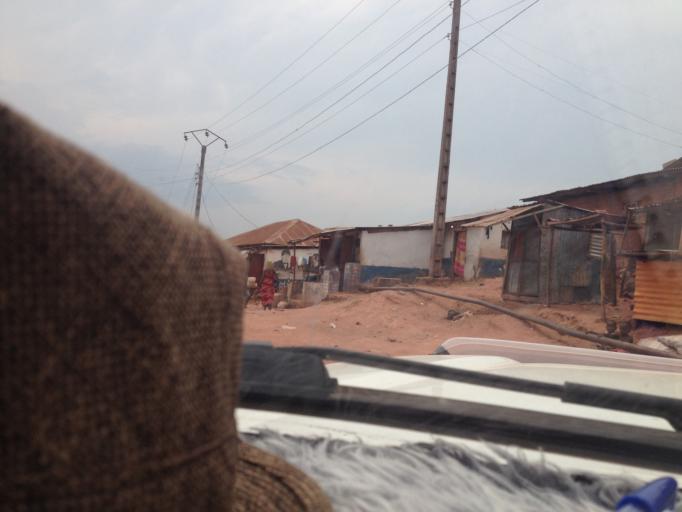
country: CD
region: Katanga
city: Kalemie
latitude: -5.9349
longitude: 29.1796
